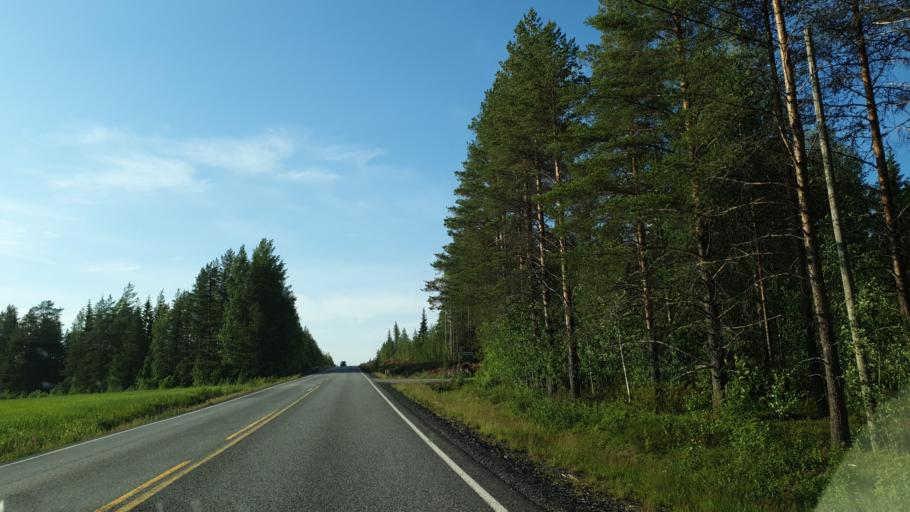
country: FI
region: Kainuu
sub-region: Kehys-Kainuu
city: Kuhmo
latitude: 64.0823
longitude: 29.4850
